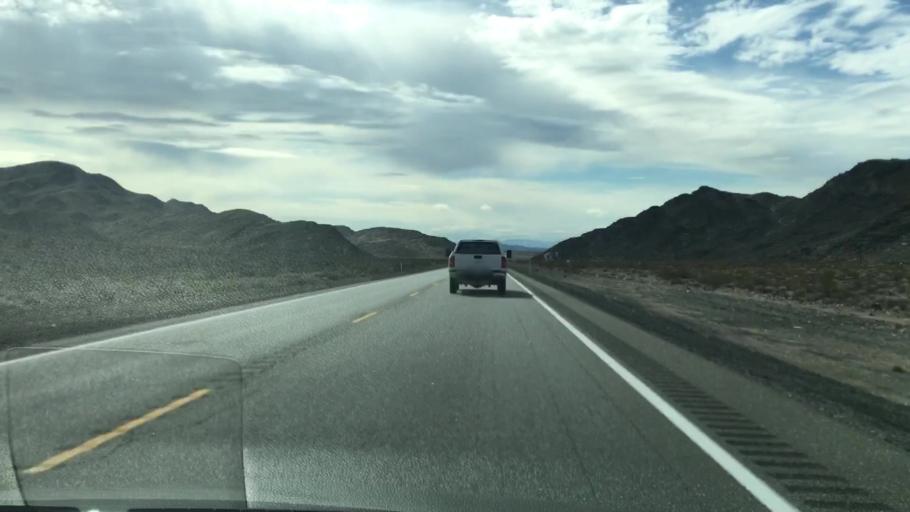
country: US
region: Nevada
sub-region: Nye County
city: Pahrump
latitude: 36.5780
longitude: -116.0695
